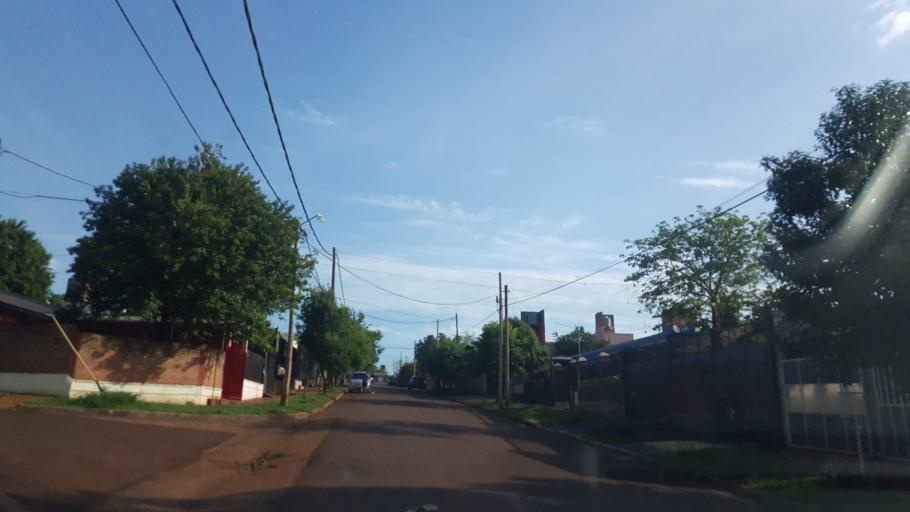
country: AR
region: Misiones
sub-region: Departamento de Capital
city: Posadas
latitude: -27.4246
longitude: -55.9238
